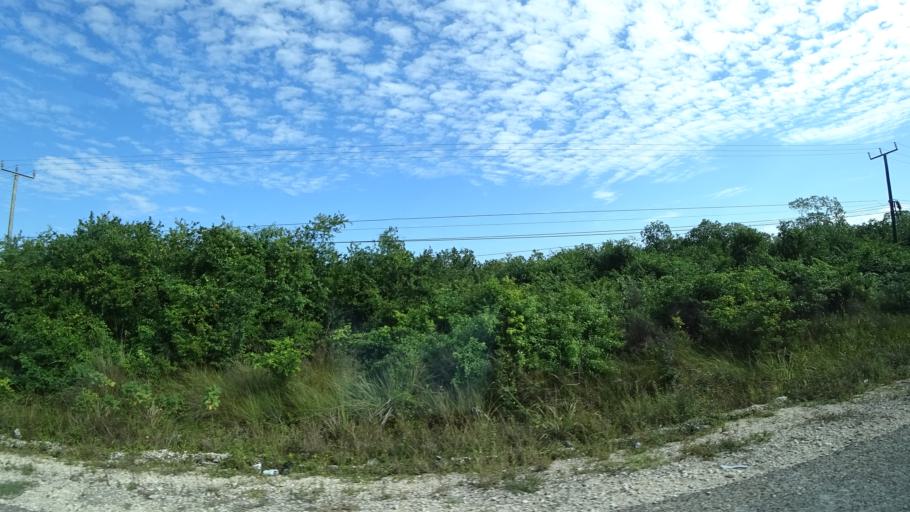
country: BZ
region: Belize
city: Belize City
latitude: 17.5430
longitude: -88.2550
